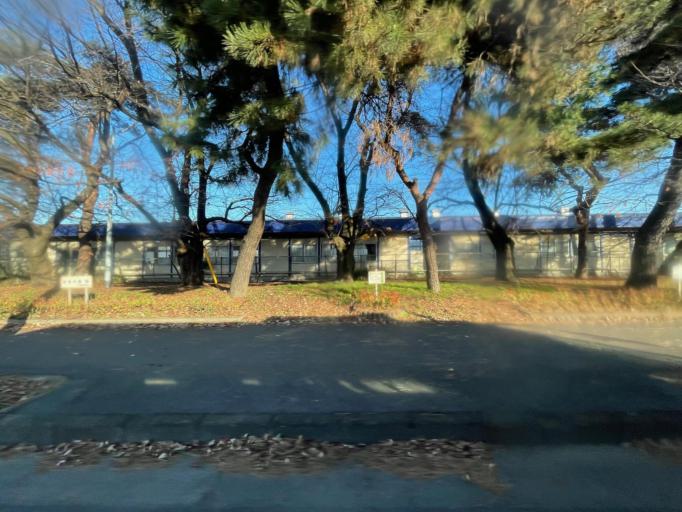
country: JP
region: Ibaraki
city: Koga
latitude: 36.1938
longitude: 139.7485
